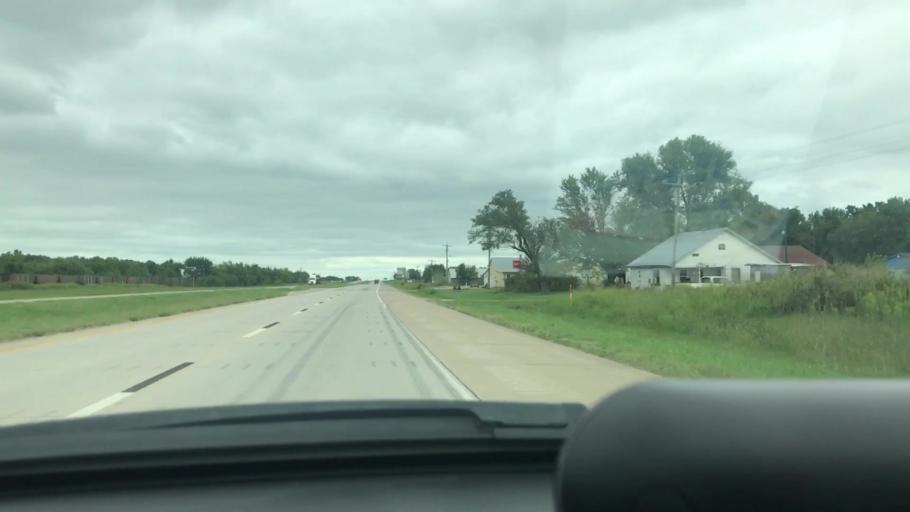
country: US
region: Oklahoma
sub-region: Mayes County
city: Chouteau
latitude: 36.0988
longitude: -95.3627
